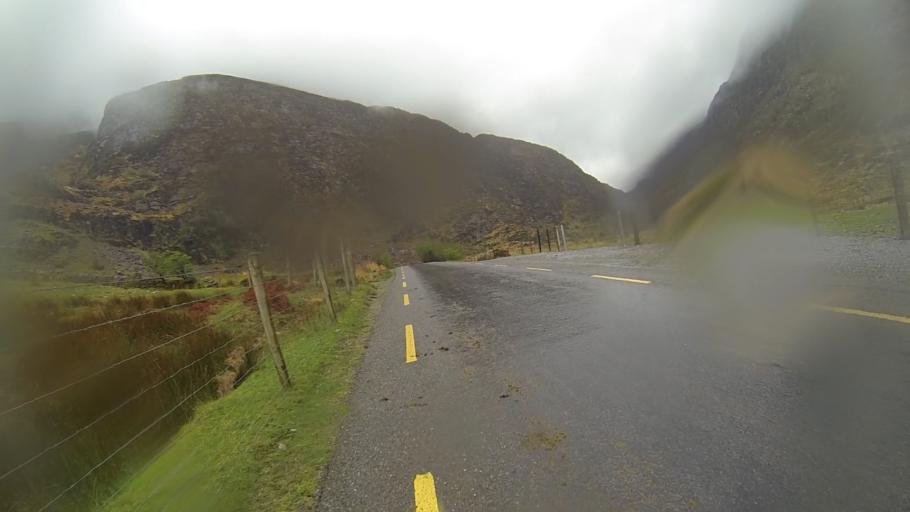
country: IE
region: Munster
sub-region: Ciarrai
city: Cill Airne
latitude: 52.0164
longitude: -9.6355
